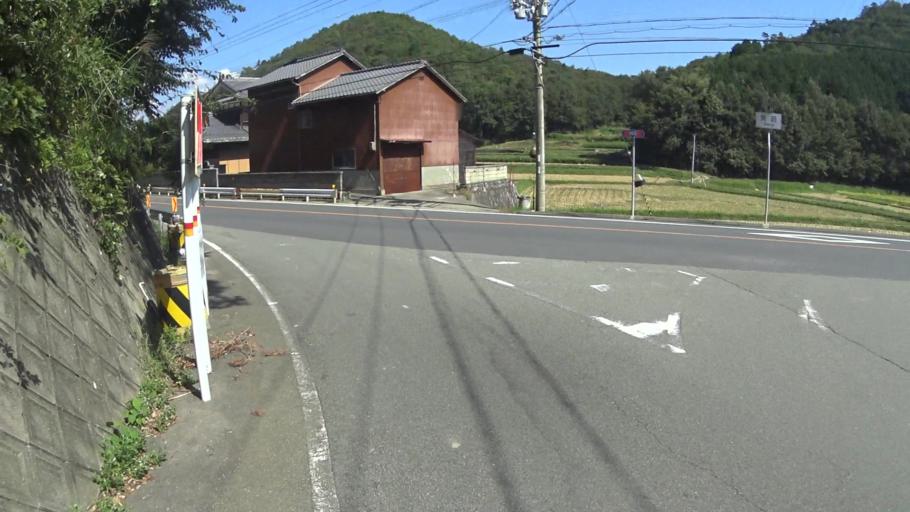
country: JP
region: Kyoto
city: Kameoka
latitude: 34.9726
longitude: 135.5174
